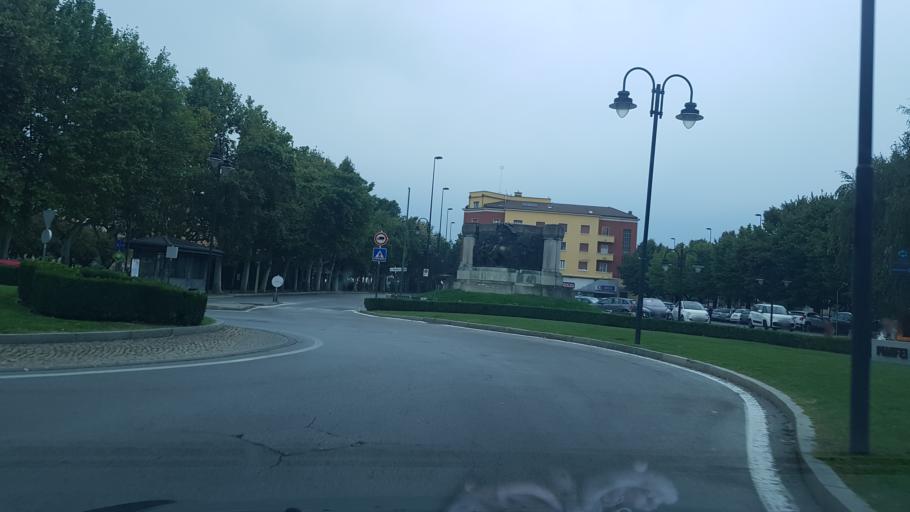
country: IT
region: Piedmont
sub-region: Provincia di Cuneo
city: Mondovi
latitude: 44.3903
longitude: 7.8195
